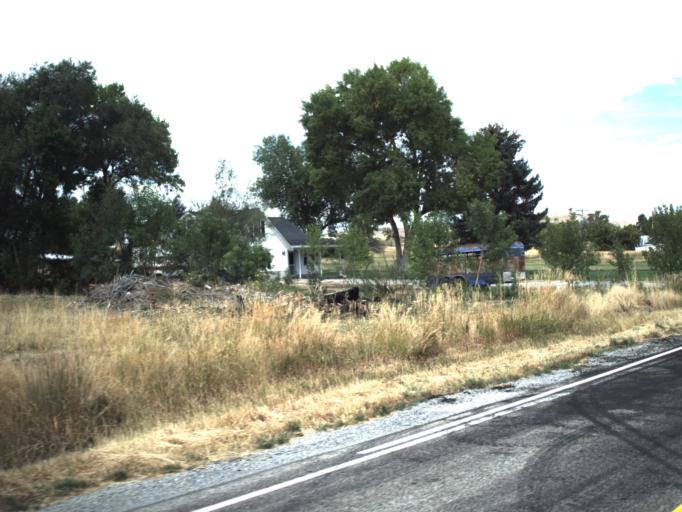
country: US
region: Utah
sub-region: Cache County
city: Mendon
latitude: 41.7430
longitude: -111.9793
